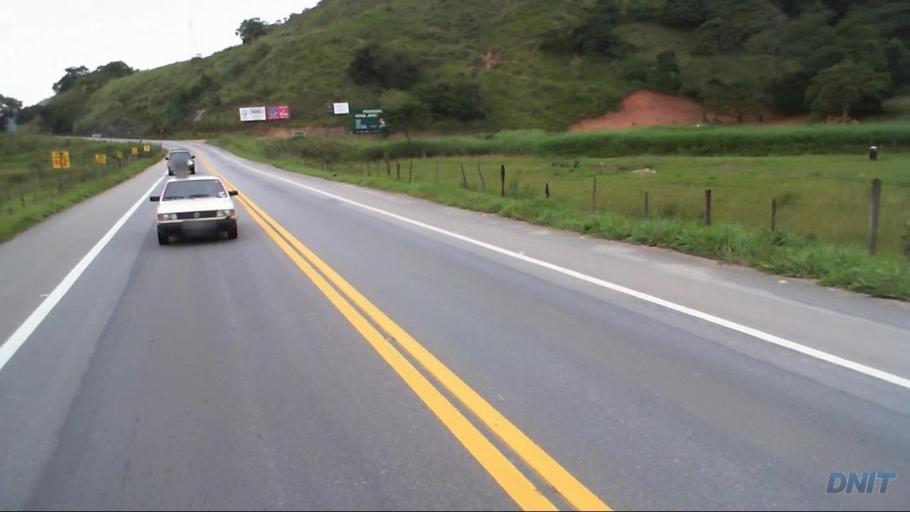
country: BR
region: Minas Gerais
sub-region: Timoteo
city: Timoteo
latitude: -19.5856
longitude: -42.7306
